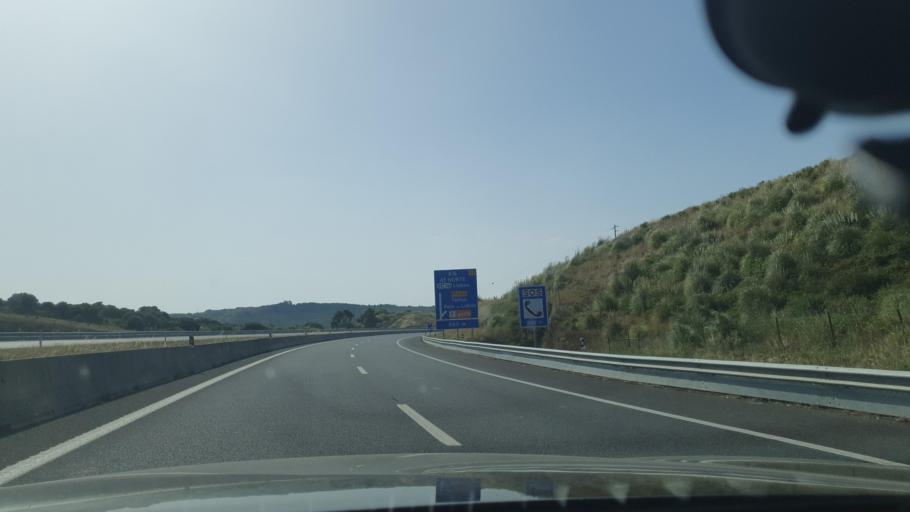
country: PT
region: Lisbon
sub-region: Sintra
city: Rio de Mouro
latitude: 38.8132
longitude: -9.3162
